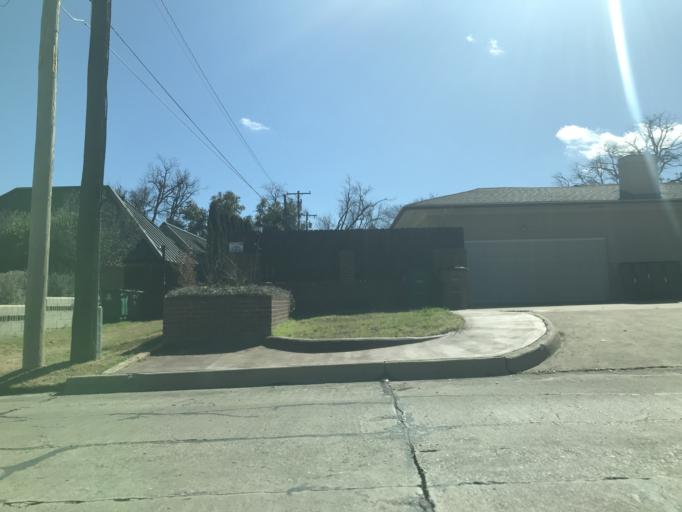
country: US
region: Texas
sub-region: Tom Green County
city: San Angelo
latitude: 31.4474
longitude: -100.4516
